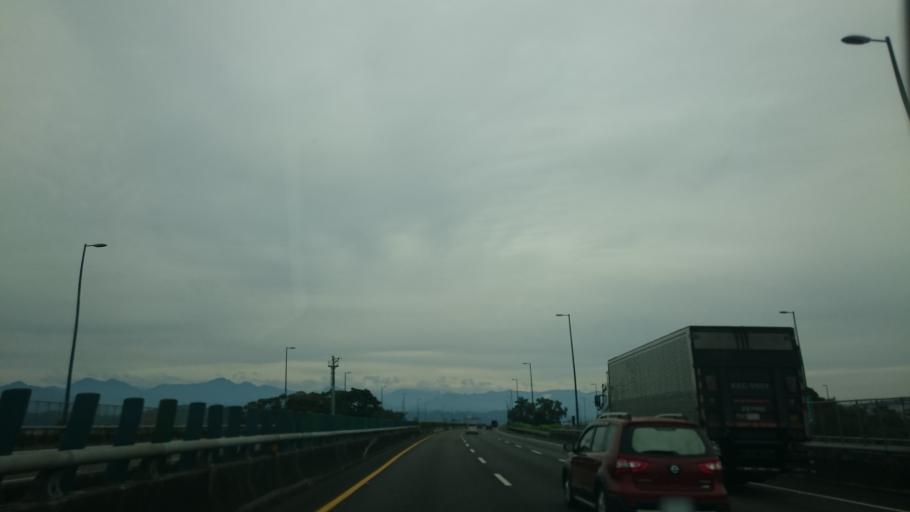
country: TW
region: Taiwan
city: Zhongxing New Village
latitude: 23.9490
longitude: 120.6689
